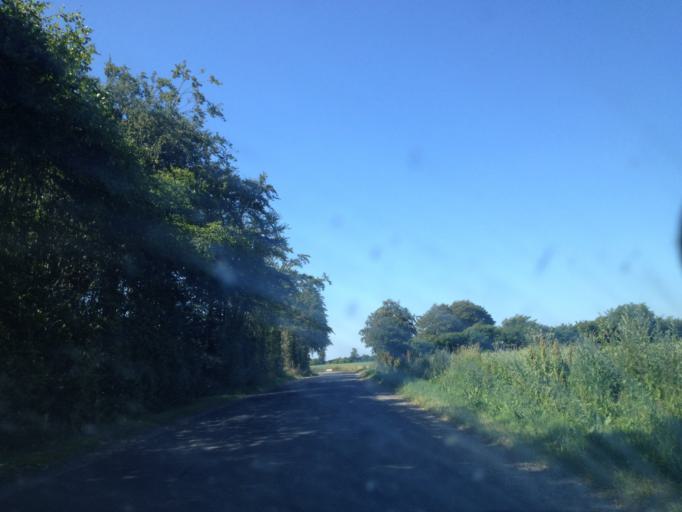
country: DK
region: South Denmark
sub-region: Kolding Kommune
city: Christiansfeld
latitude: 55.4029
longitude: 9.5170
